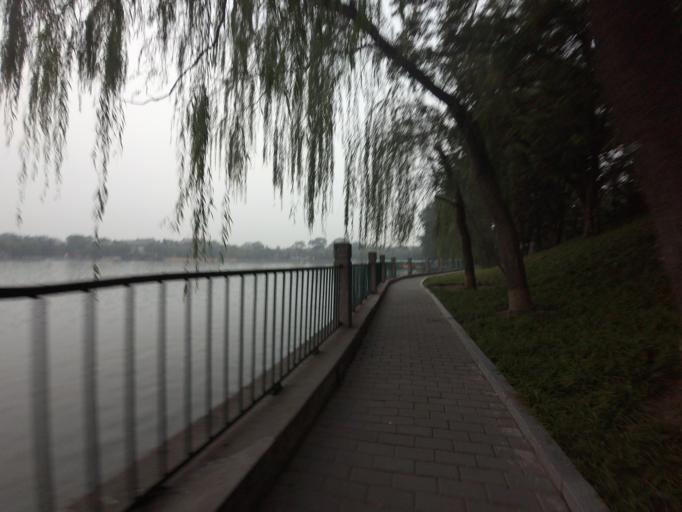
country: CN
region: Beijing
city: Jingshan
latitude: 39.9291
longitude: 116.3851
